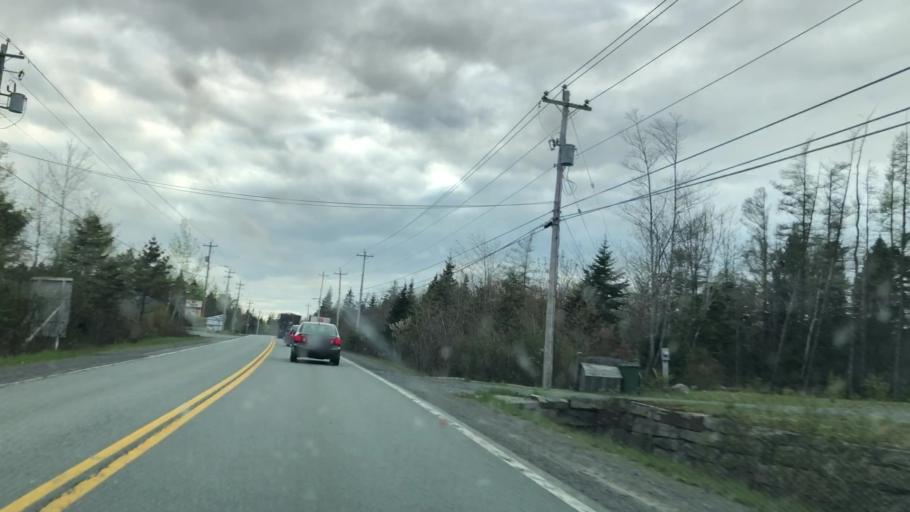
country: CA
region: Nova Scotia
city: Cole Harbour
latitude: 44.7829
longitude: -63.1715
